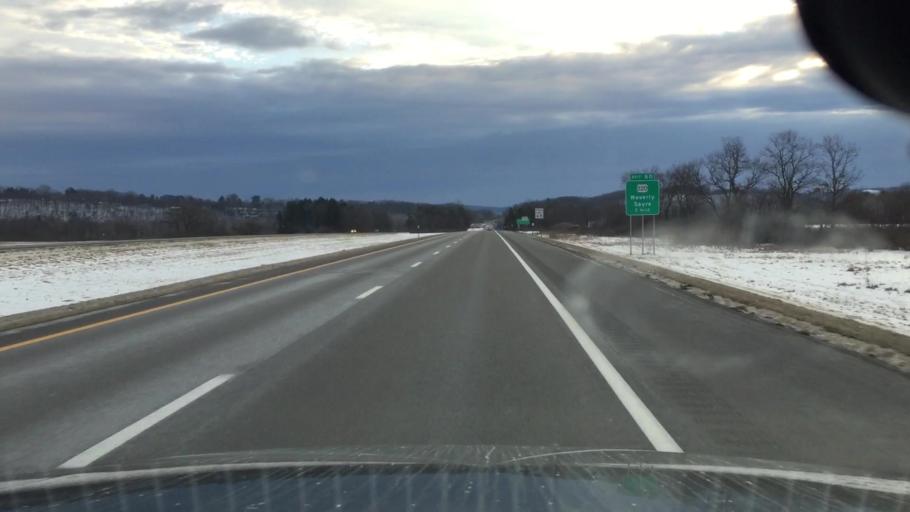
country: US
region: Pennsylvania
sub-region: Bradford County
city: South Waverly
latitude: 42.0006
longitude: -76.5767
